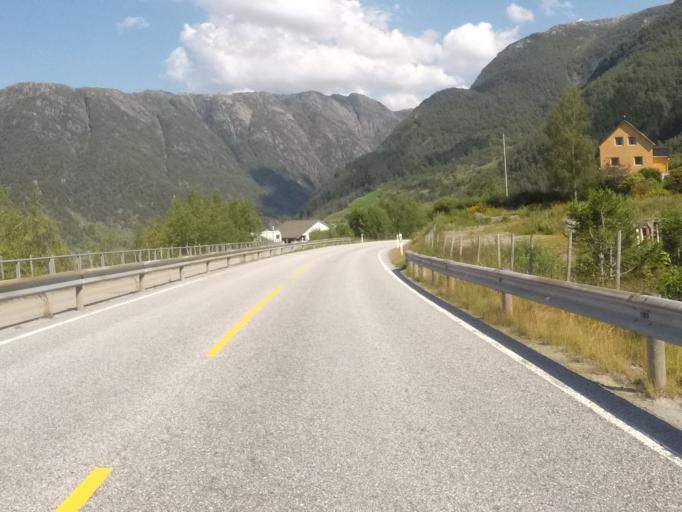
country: NO
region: Hordaland
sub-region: Masfjorden
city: Masfjorden
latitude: 60.9000
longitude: 5.5219
